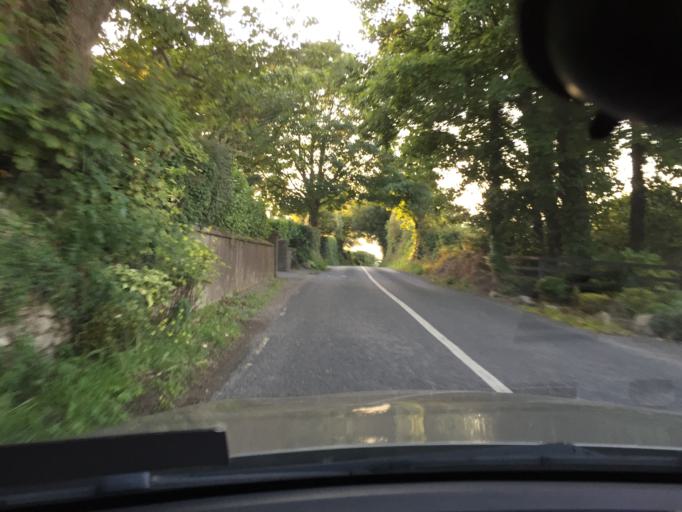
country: IE
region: Leinster
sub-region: Wicklow
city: Enniskerry
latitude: 53.1675
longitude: -6.1767
